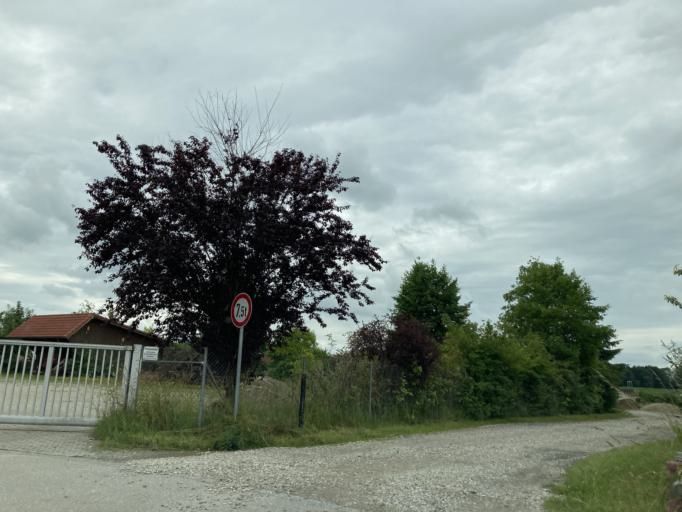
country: DE
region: Bavaria
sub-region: Upper Bavaria
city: Vogtareuth
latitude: 47.9537
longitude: 12.1781
